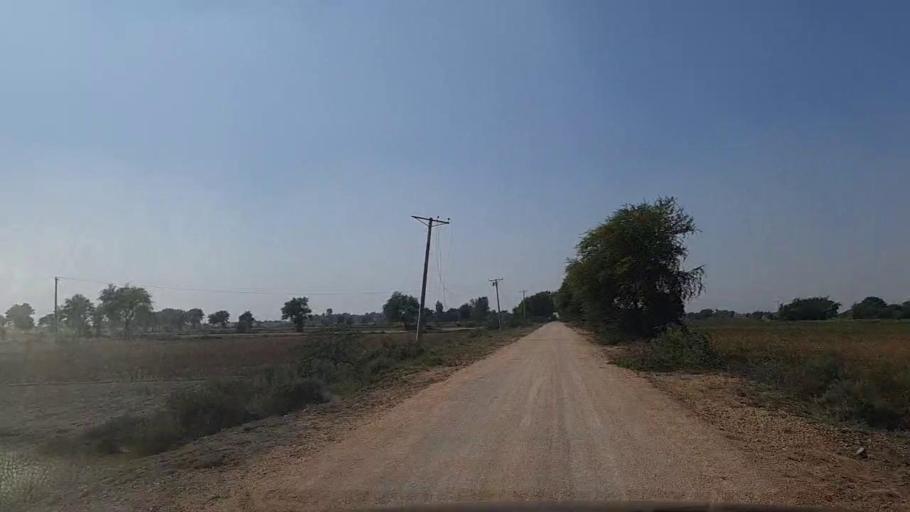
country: PK
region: Sindh
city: Daro Mehar
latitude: 24.8365
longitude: 68.1557
